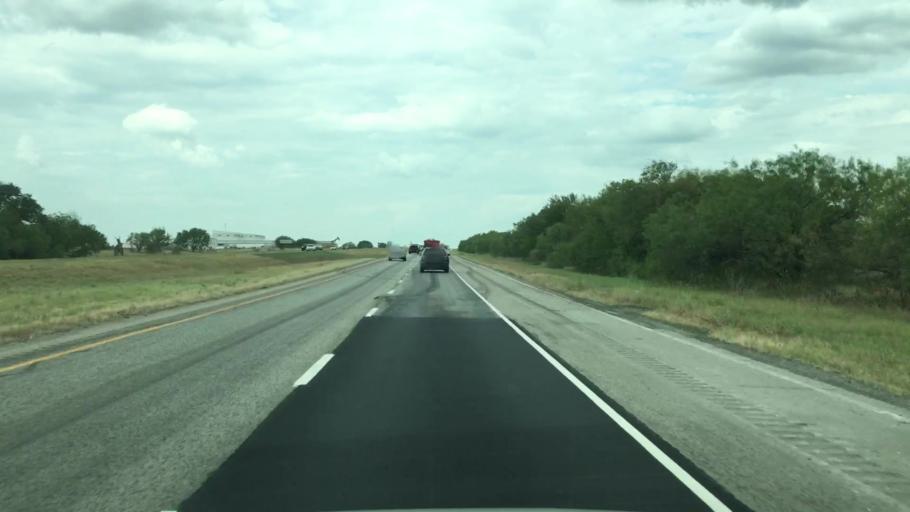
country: US
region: Texas
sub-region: Atascosa County
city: Pleasanton
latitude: 29.0904
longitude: -98.4328
